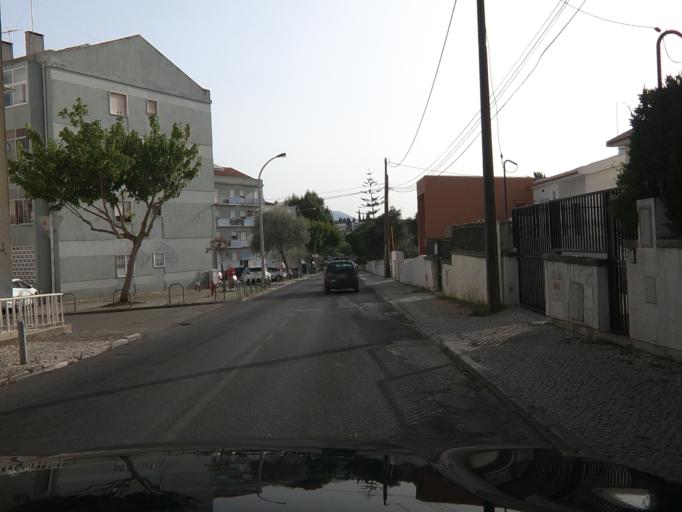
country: PT
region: Setubal
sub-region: Setubal
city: Setubal
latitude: 38.5413
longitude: -8.8957
